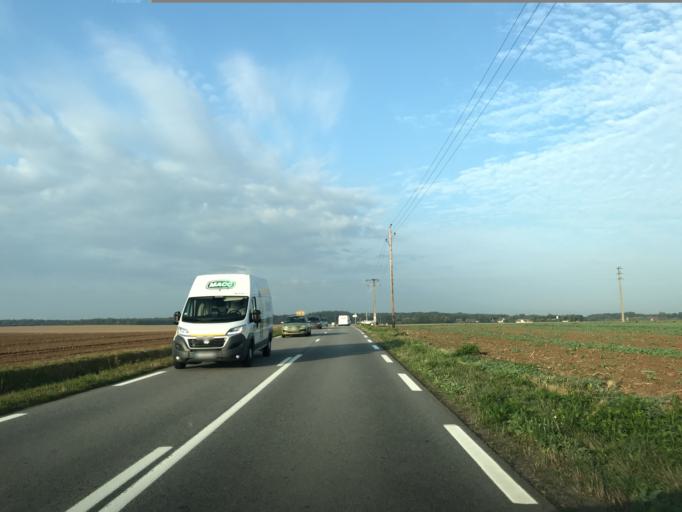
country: FR
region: Haute-Normandie
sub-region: Departement de l'Eure
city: Gravigny
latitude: 49.0689
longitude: 1.2138
